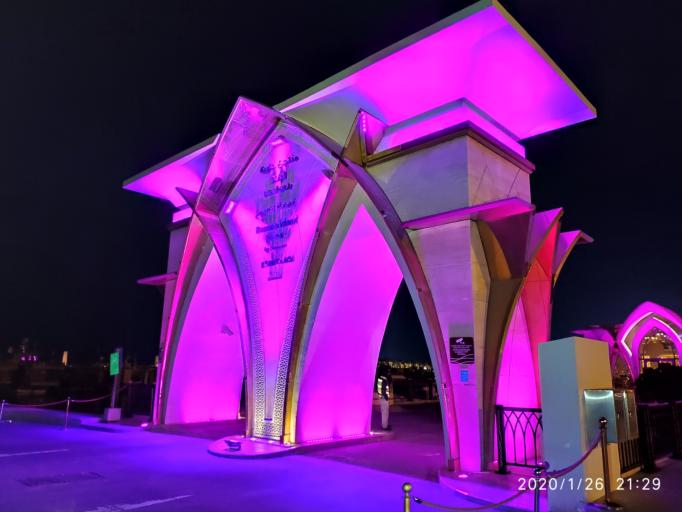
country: QA
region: Baladiyat ad Dawhah
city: Doha
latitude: 25.2921
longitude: 51.5343
